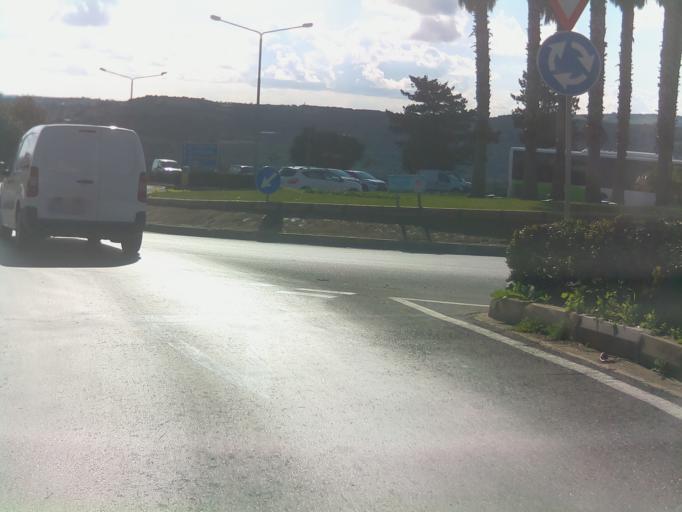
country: MT
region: Il-Mellieha
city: Mellieha
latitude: 35.9546
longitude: 14.3721
